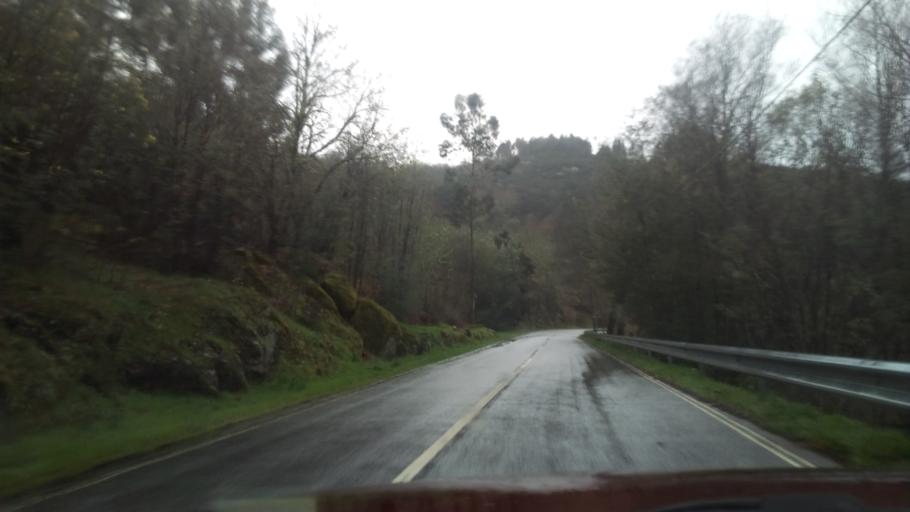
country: PT
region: Guarda
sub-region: Fornos de Algodres
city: Fornos de Algodres
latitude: 40.6166
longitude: -7.5014
